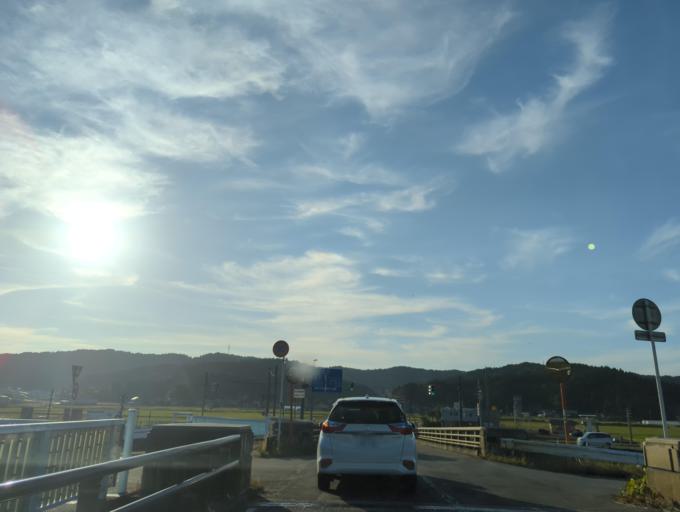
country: JP
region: Niigata
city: Nagaoka
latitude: 37.5530
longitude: 138.8166
